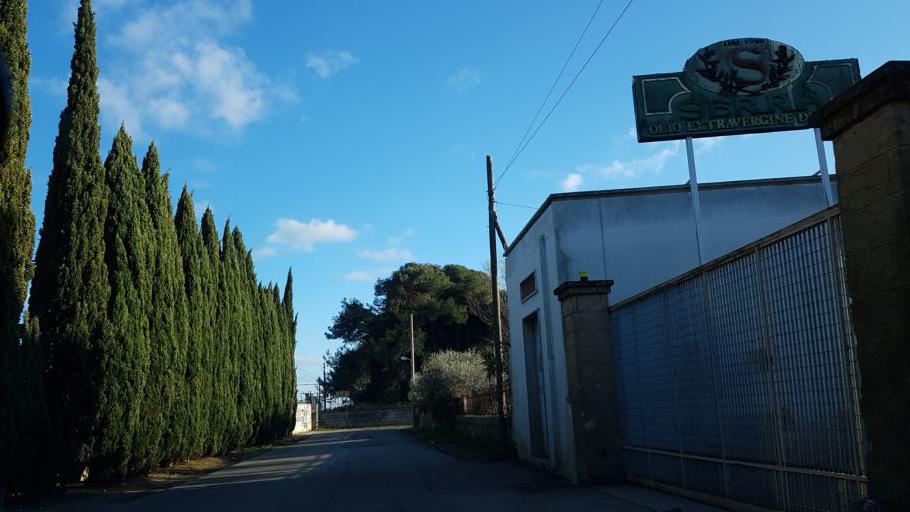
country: IT
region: Apulia
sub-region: Provincia di Lecce
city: Squinzano
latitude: 40.4426
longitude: 18.0421
